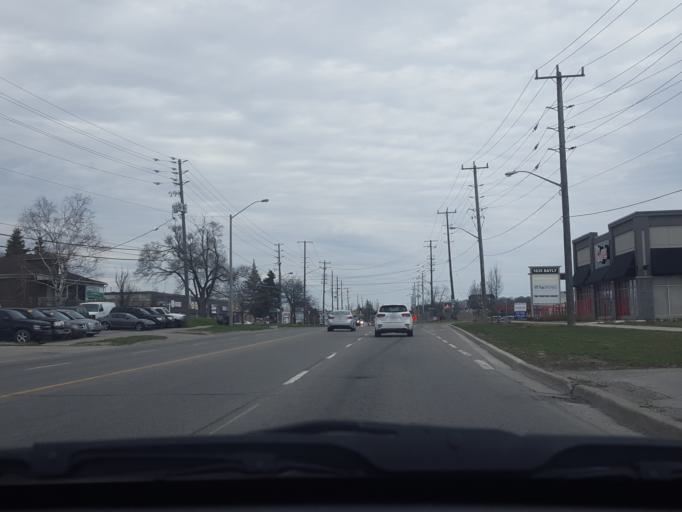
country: CA
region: Ontario
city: Ajax
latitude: 43.8320
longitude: -79.0722
